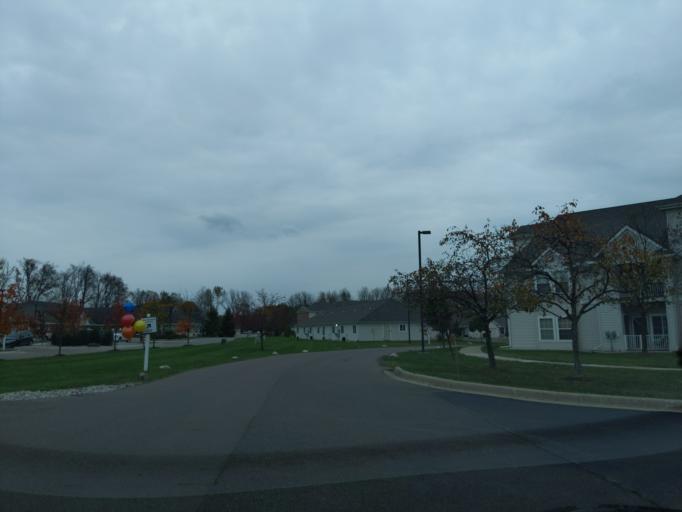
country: US
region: Michigan
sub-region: Ingham County
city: Edgemont Park
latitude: 42.7102
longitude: -84.5930
